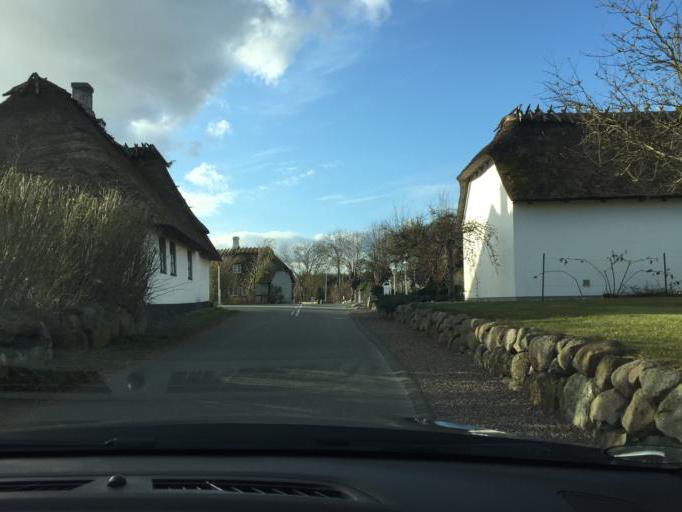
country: DK
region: South Denmark
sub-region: Kerteminde Kommune
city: Langeskov
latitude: 55.3436
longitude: 10.6079
